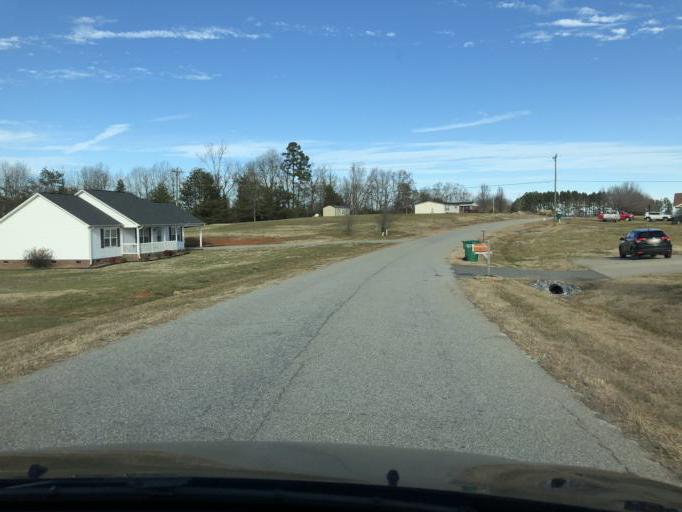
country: US
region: South Carolina
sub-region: Cherokee County
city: East Gaffney
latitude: 35.1386
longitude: -81.6681
